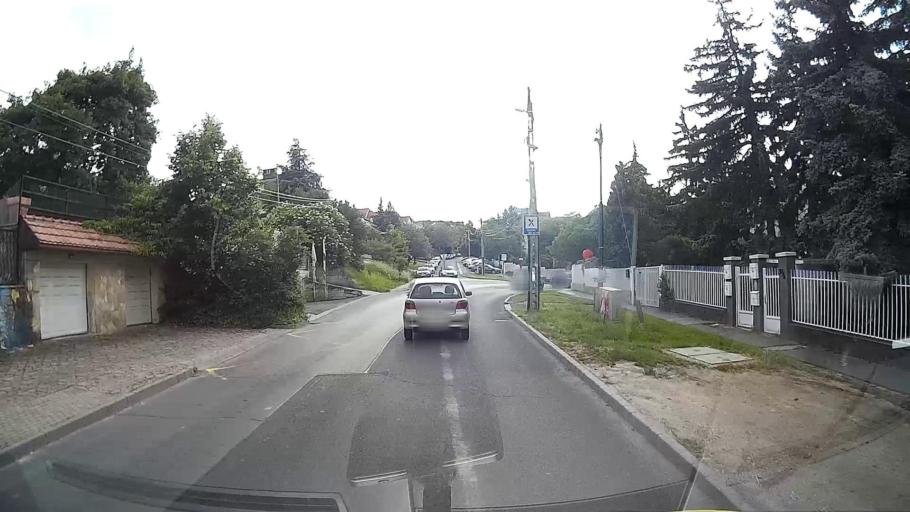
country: HU
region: Budapest
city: Budapest II. keruelet
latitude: 47.5286
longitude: 19.0215
